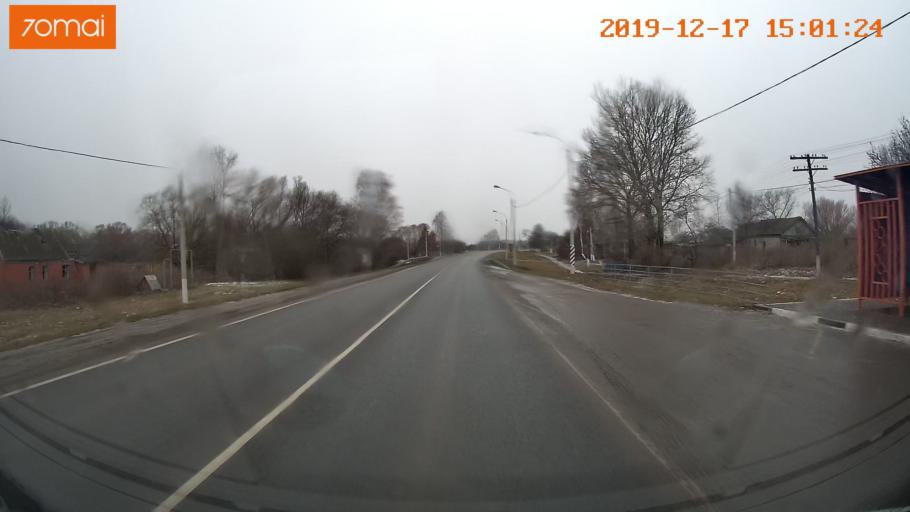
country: RU
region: Rjazan
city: Zakharovo
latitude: 54.2835
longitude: 39.1788
